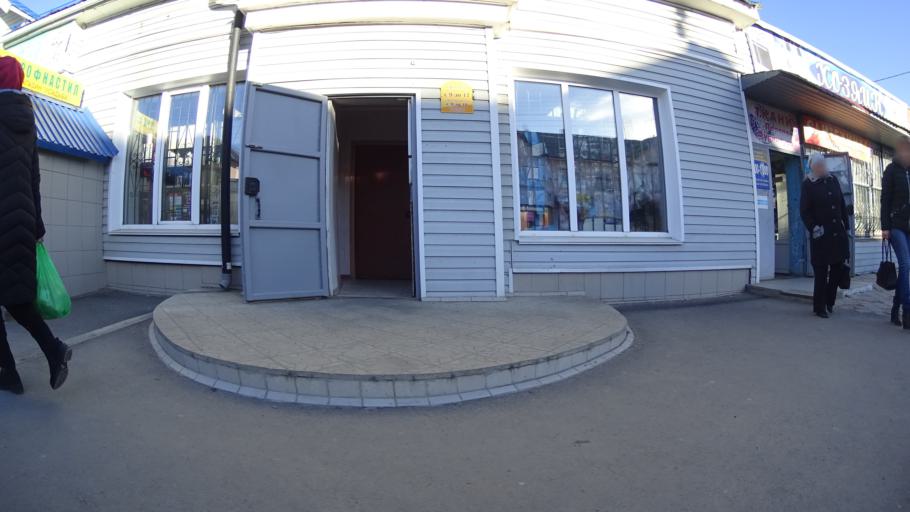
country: RU
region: Chelyabinsk
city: Troitsk
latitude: 54.0901
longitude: 61.5575
